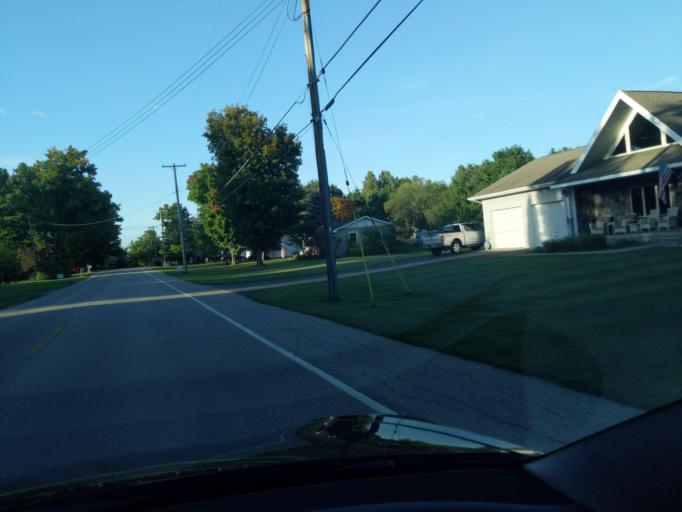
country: US
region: Michigan
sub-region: Antrim County
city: Elk Rapids
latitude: 44.8903
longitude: -85.4223
